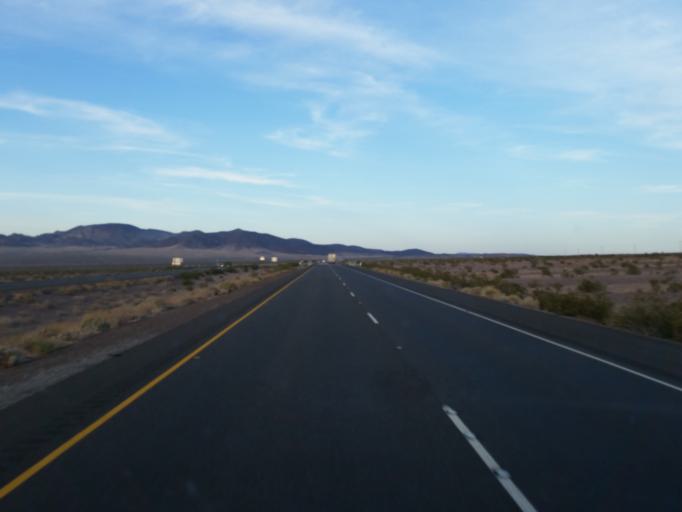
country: US
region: California
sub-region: San Bernardino County
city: Twentynine Palms
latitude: 34.7260
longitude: -116.1485
